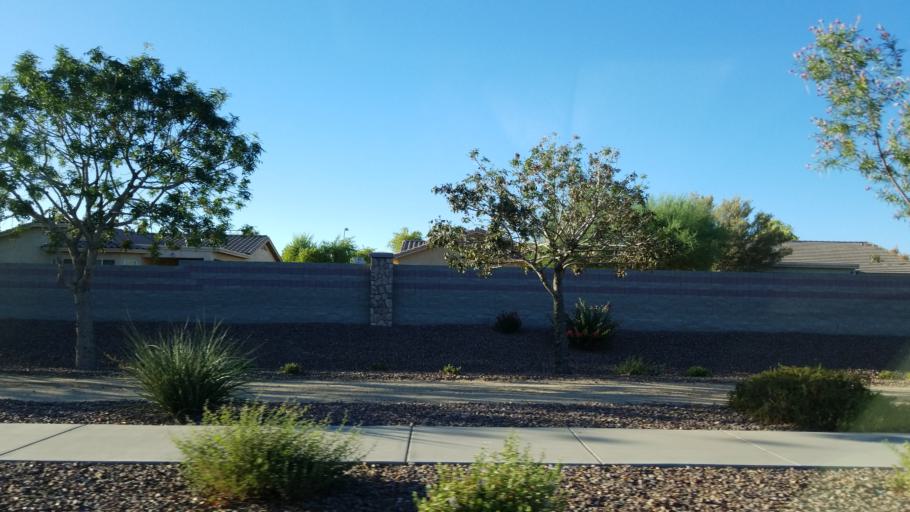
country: US
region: Arizona
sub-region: Maricopa County
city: Laveen
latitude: 33.3775
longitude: -112.2157
